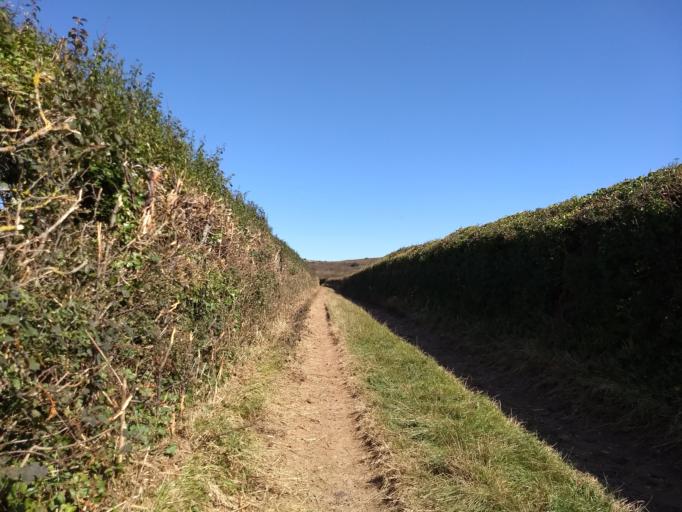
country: GB
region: England
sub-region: Isle of Wight
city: Shalfleet
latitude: 50.6456
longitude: -1.4323
